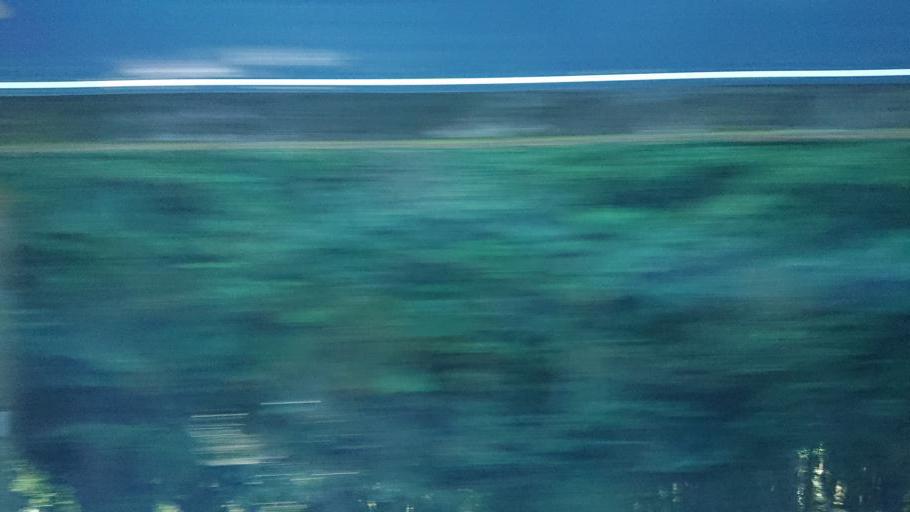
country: TW
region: Taiwan
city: Lugu
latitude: 23.4919
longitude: 120.8192
